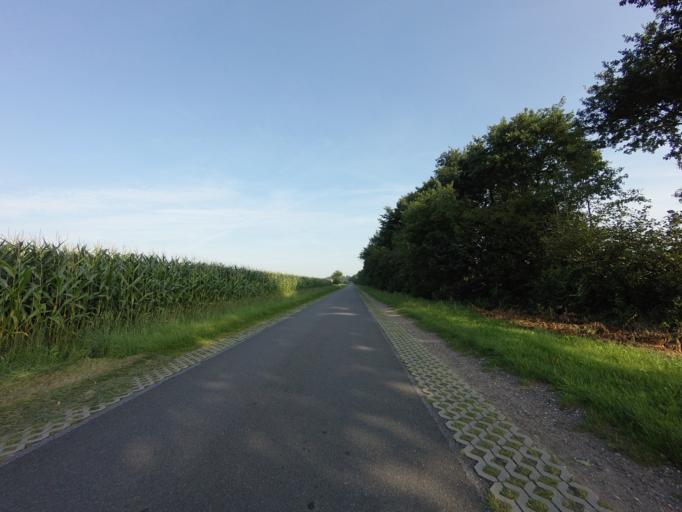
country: DE
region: Lower Saxony
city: Itterbeck
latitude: 52.4813
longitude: 6.8189
